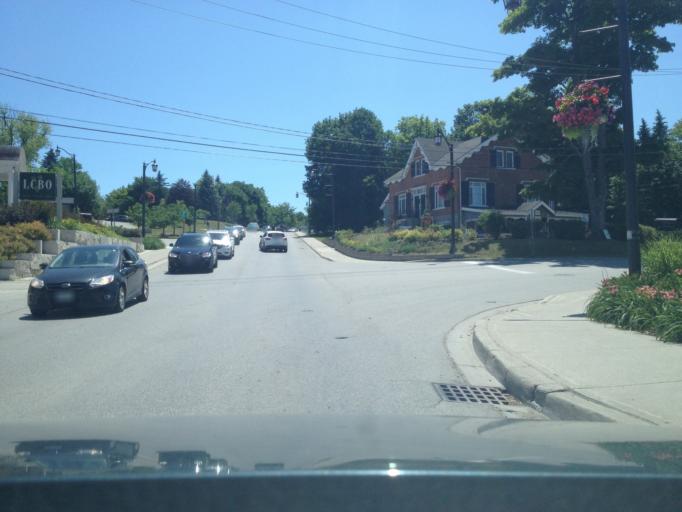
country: CA
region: Ontario
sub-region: Wellington County
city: Guelph
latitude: 43.6802
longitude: -80.4293
